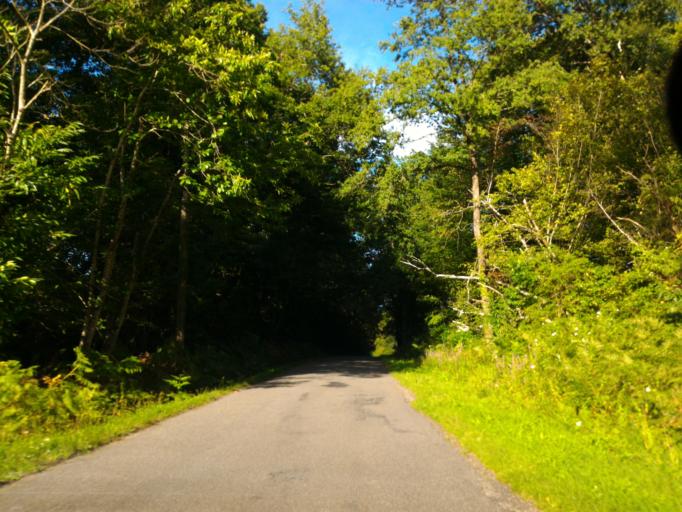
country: FR
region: Poitou-Charentes
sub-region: Departement de la Charente
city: Brigueuil
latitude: 45.9858
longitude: 0.8261
